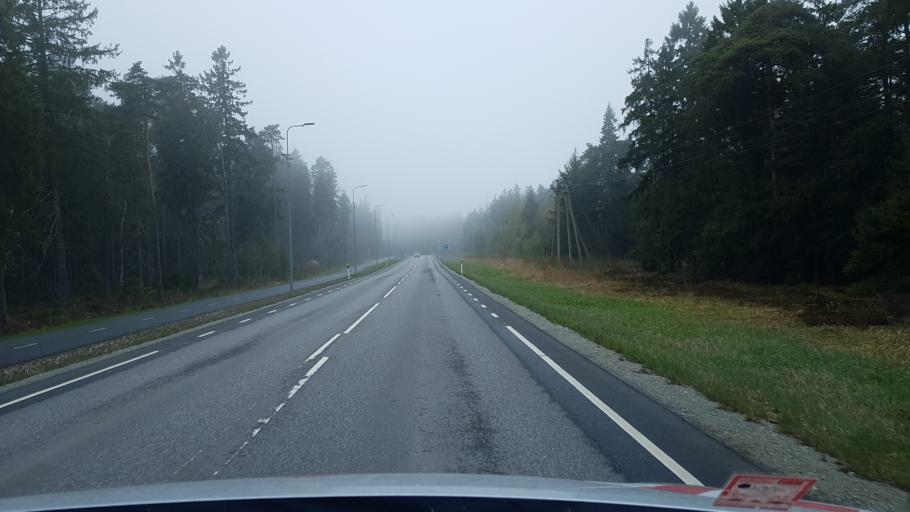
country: EE
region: Harju
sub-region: Viimsi vald
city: Viimsi
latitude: 59.5188
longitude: 24.8981
